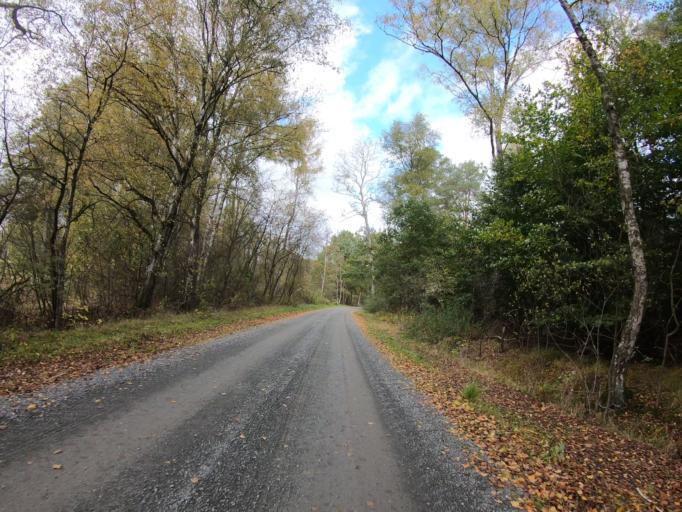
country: DE
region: Lower Saxony
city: Wesendorf
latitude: 52.5671
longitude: 10.5640
